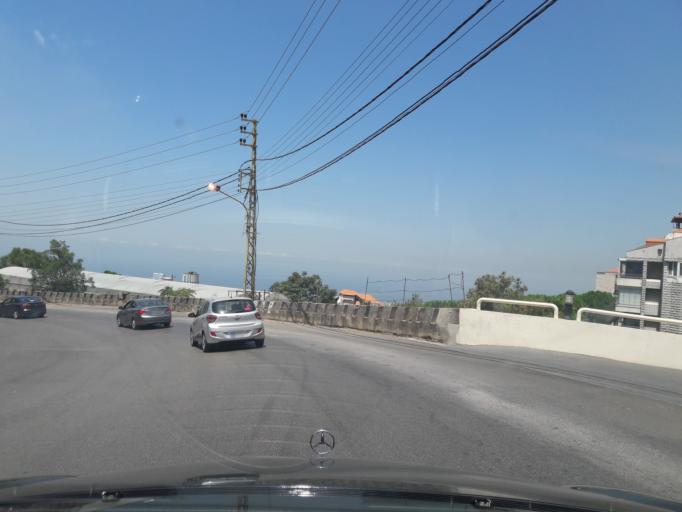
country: LB
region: Mont-Liban
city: Djounie
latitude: 33.9266
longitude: 35.6369
